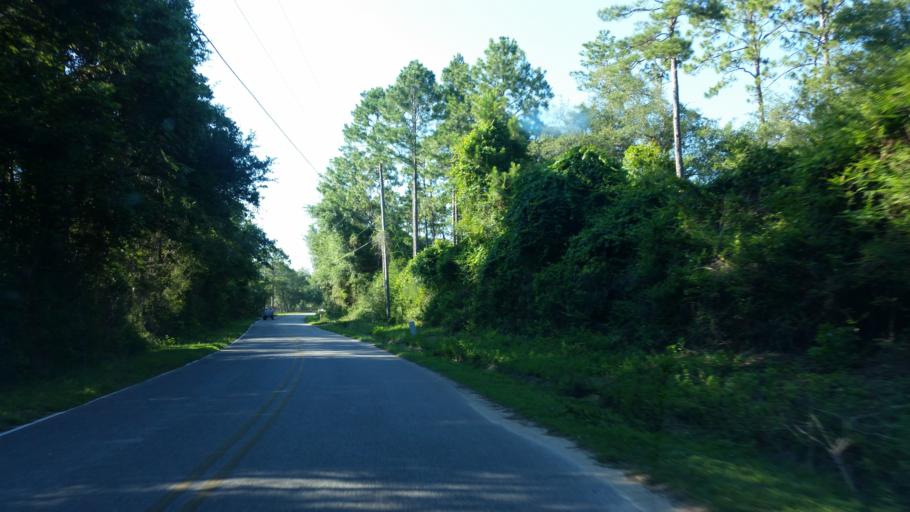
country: US
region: Florida
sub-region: Escambia County
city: Bellview
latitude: 30.4921
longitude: -87.3842
